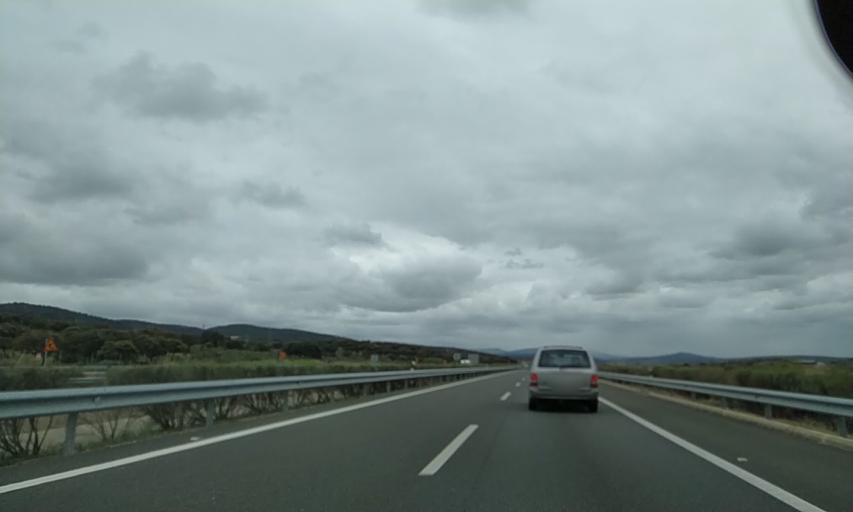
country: ES
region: Extremadura
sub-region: Provincia de Caceres
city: Carcaboso
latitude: 39.9670
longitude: -6.1641
